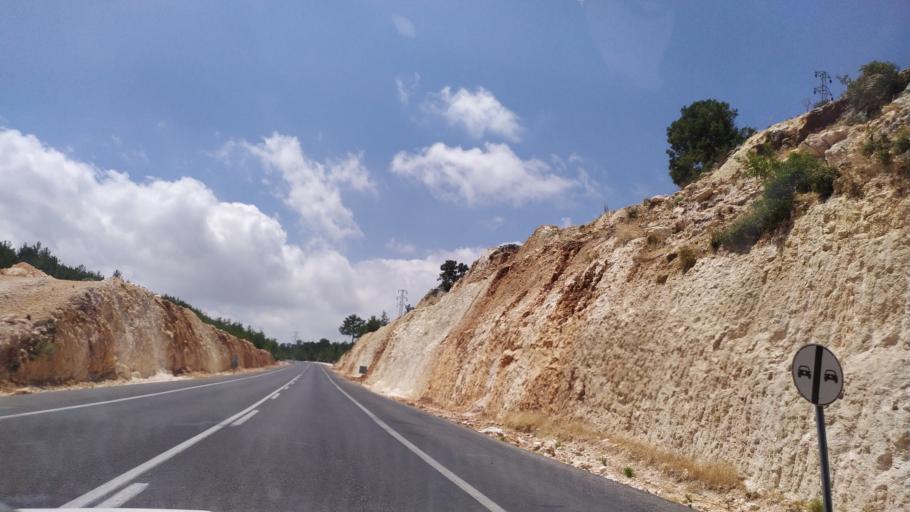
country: TR
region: Mersin
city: Gulnar
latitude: 36.2746
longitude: 33.3768
